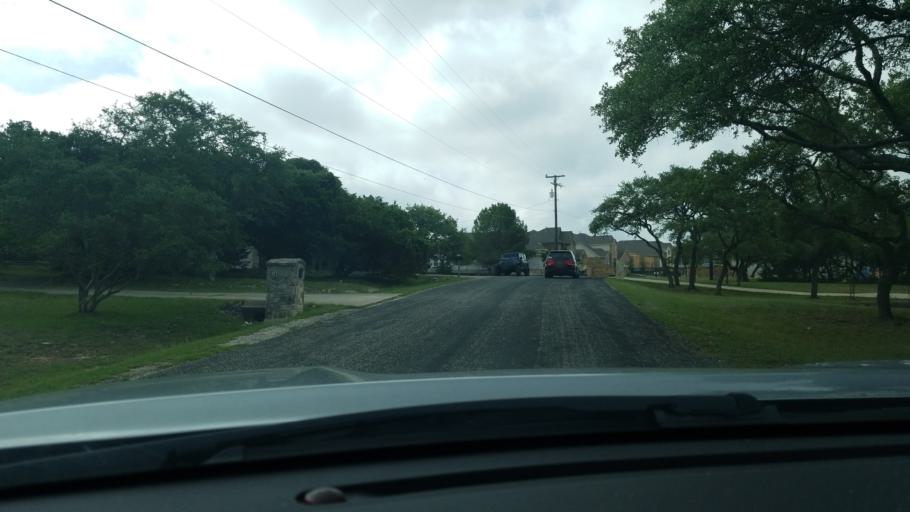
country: US
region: Texas
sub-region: Bexar County
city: Timberwood Park
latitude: 29.6855
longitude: -98.4793
